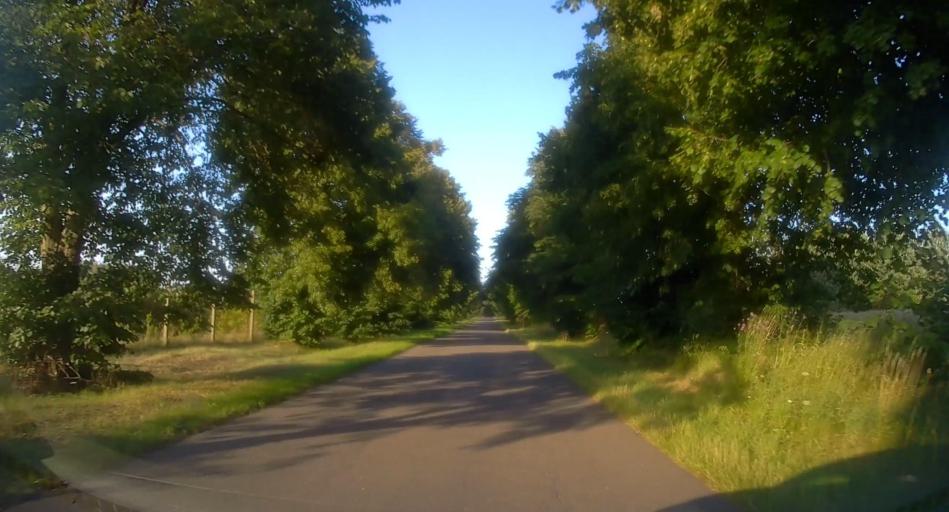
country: PL
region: Lodz Voivodeship
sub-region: Powiat skierniewicki
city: Kaweczyn Nowy
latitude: 51.9045
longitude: 20.3202
